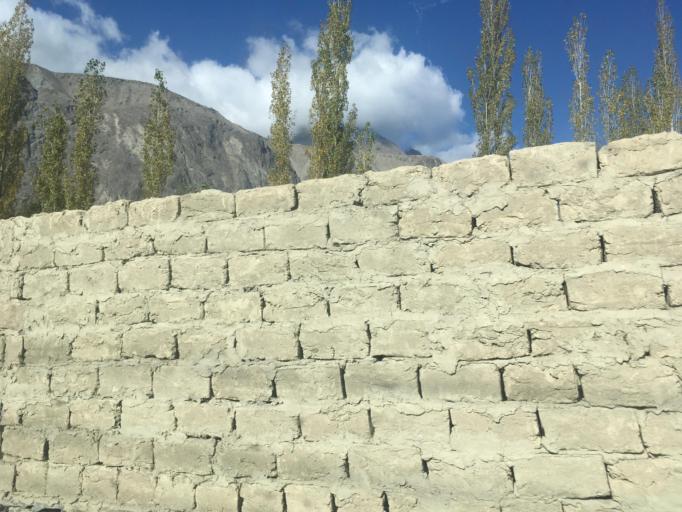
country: PK
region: Gilgit-Baltistan
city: Skardu
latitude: 35.3475
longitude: 75.5223
